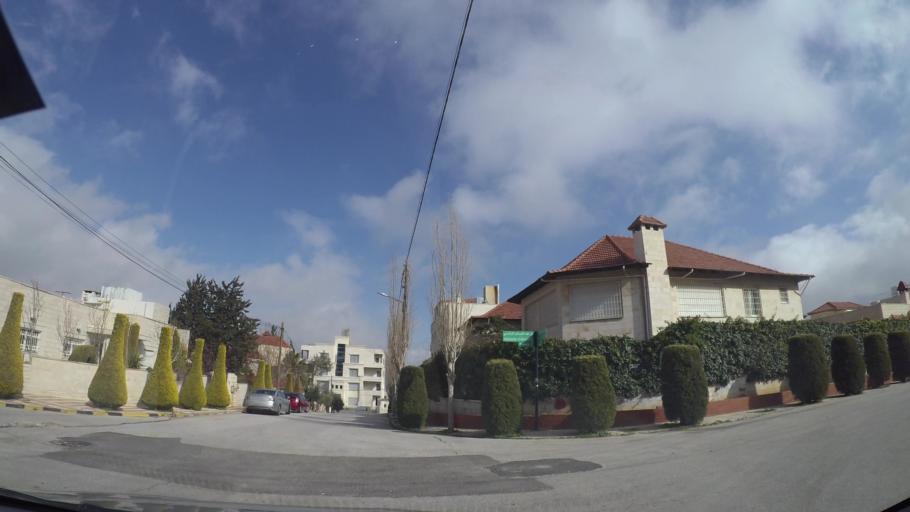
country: JO
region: Amman
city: Al Jubayhah
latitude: 32.0419
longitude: 35.8719
